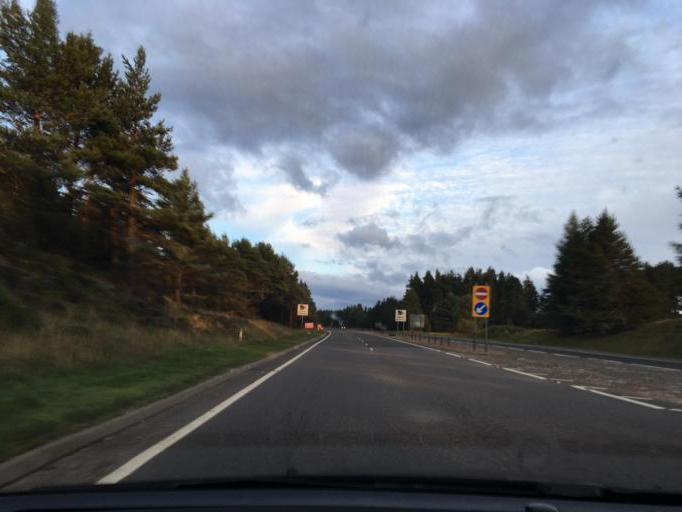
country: GB
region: Scotland
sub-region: Highland
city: Aviemore
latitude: 57.3435
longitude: -3.9986
